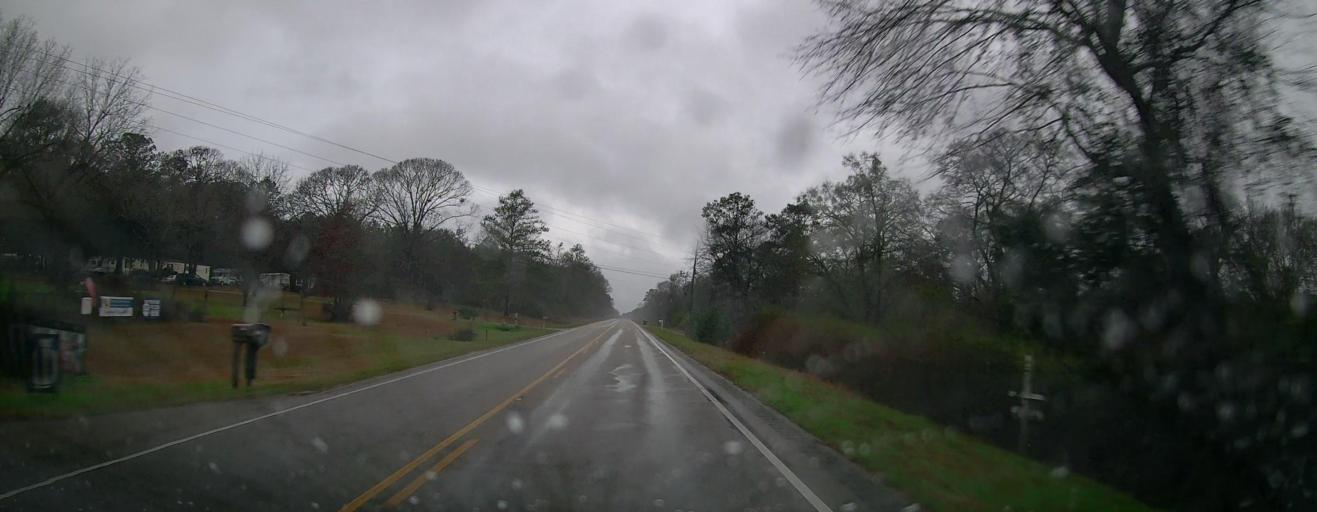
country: US
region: Alabama
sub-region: Autauga County
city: Prattville
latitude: 32.5150
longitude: -86.5923
